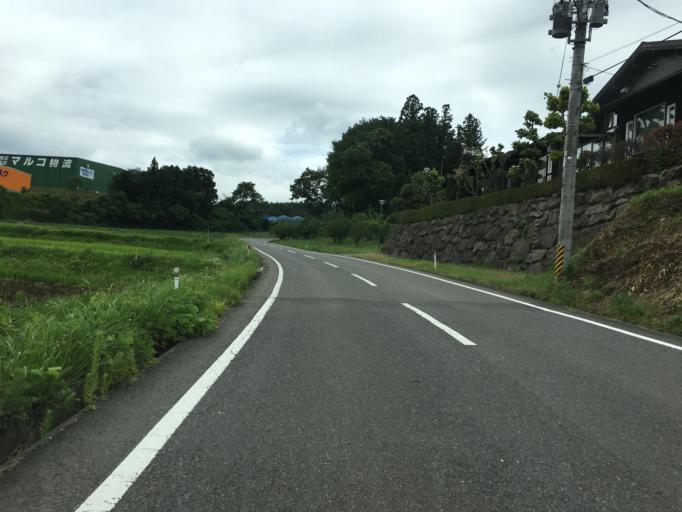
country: JP
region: Fukushima
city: Nihommatsu
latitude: 37.5777
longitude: 140.4280
